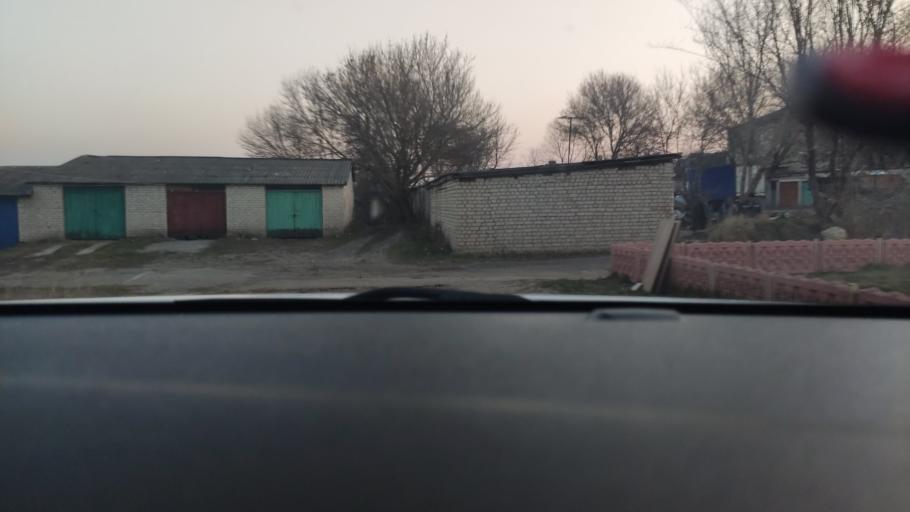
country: RU
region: Voronezj
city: Uryv-Pokrovka
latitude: 51.1110
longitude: 39.1586
